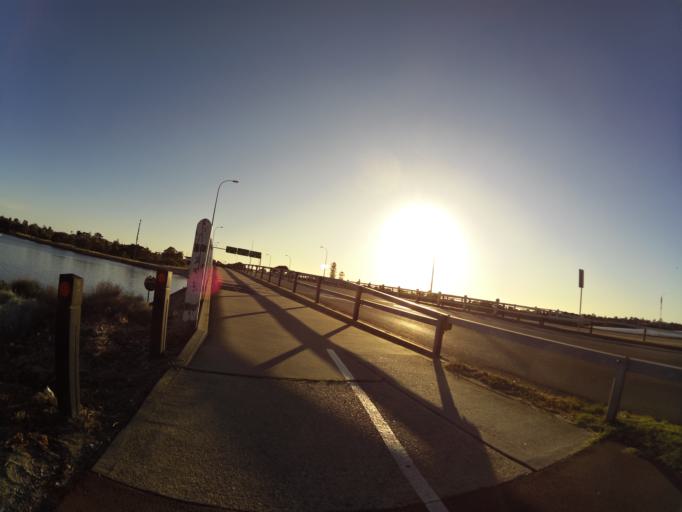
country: AU
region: Western Australia
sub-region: South Perth
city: Manning
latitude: -32.0111
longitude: 115.8523
